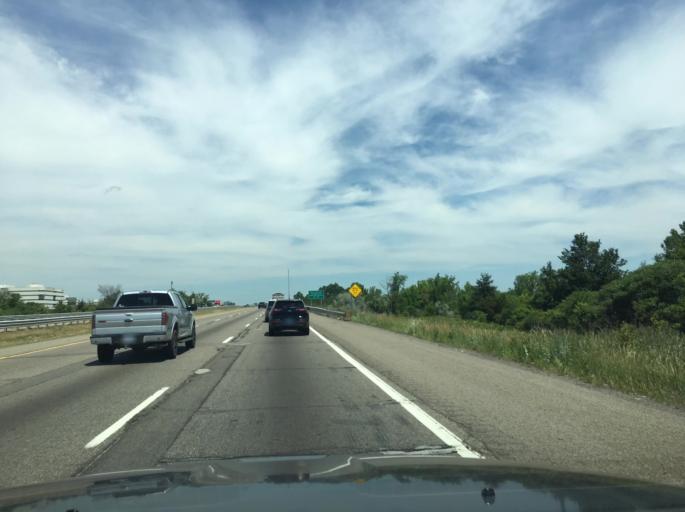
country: US
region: Michigan
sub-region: Oakland County
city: Troy
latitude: 42.5878
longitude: -83.1591
